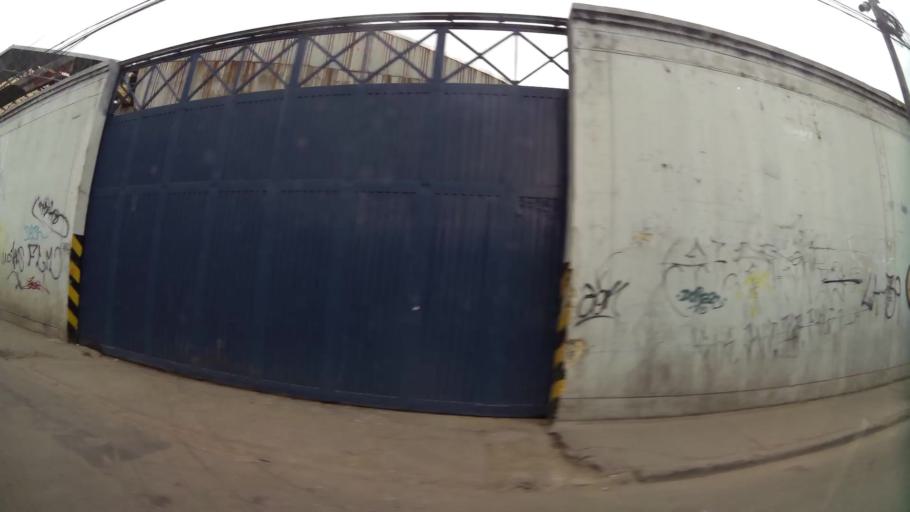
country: CO
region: Bogota D.C.
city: Bogota
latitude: 4.5975
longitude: -74.1397
